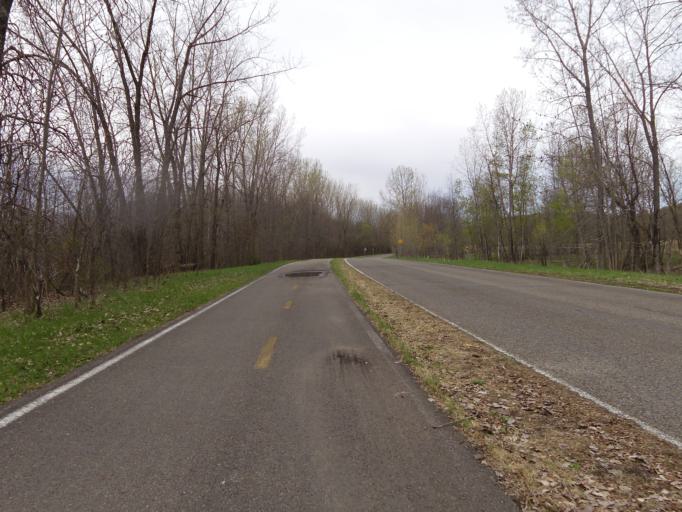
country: CA
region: Quebec
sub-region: Laurentides
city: Oka
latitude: 45.4845
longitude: -74.0232
